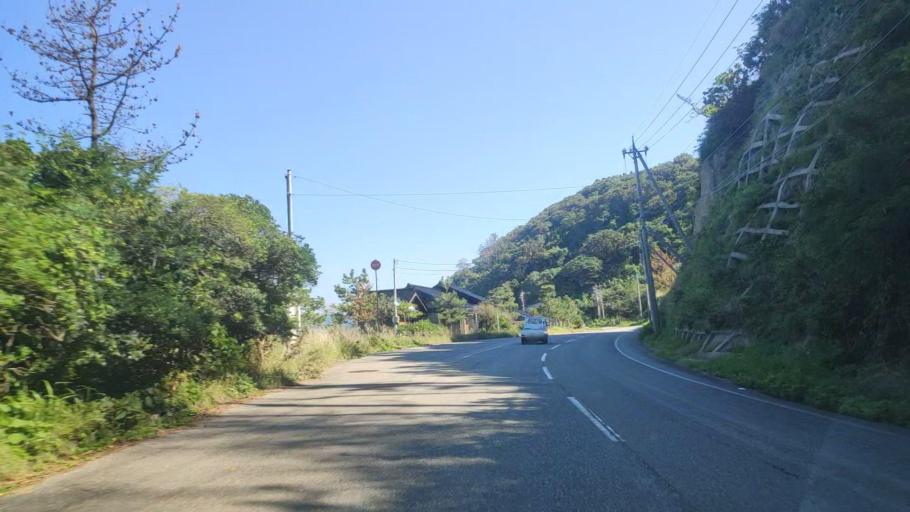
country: JP
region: Ishikawa
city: Nanao
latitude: 37.2494
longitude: 136.7152
